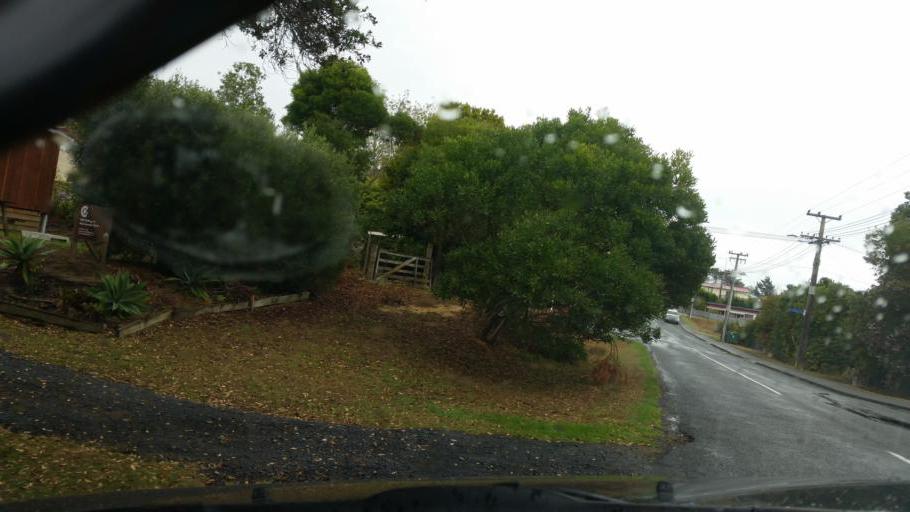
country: NZ
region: Auckland
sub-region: Auckland
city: Wellsford
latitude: -36.0939
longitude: 174.5896
